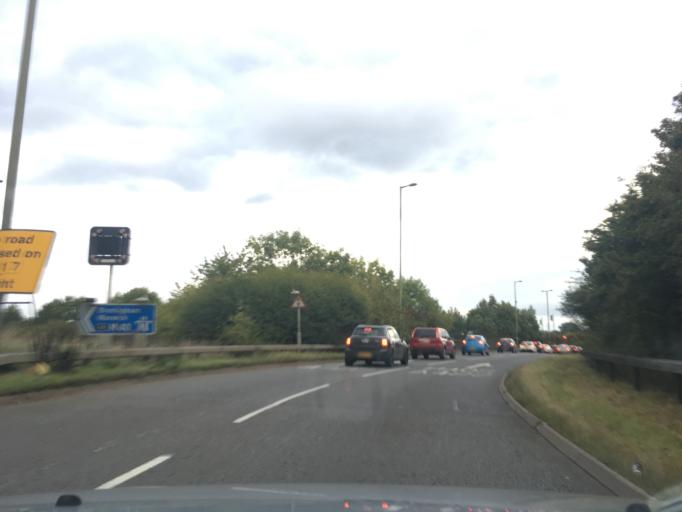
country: GB
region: England
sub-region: Oxfordshire
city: Banbury
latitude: 52.0729
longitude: -1.3146
